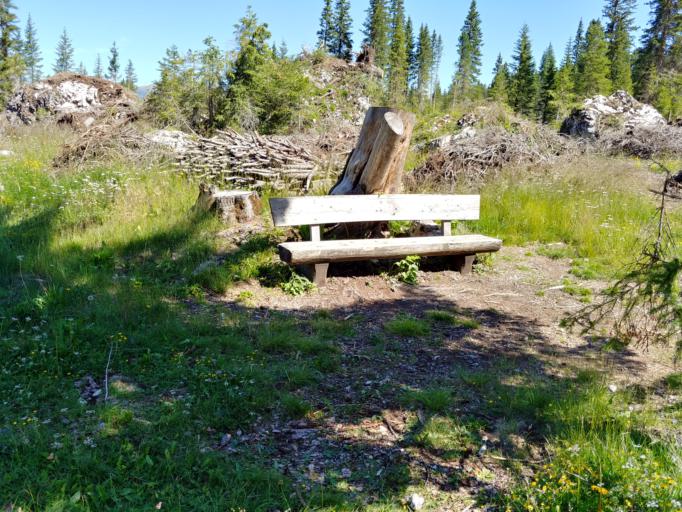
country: IT
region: Trentino-Alto Adige
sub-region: Bolzano
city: Santa Cristina Valgardena
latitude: 46.5339
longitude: 11.7032
